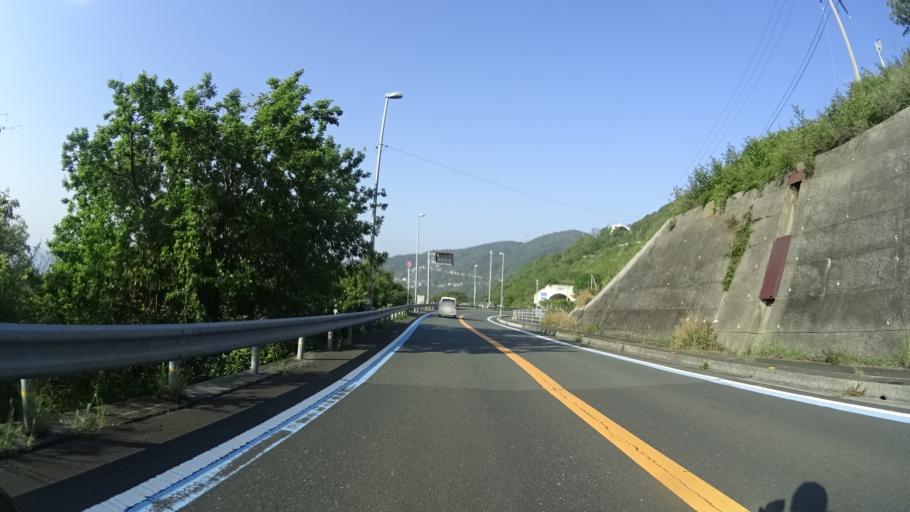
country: JP
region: Ehime
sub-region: Nishiuwa-gun
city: Ikata-cho
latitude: 33.3973
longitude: 132.1609
